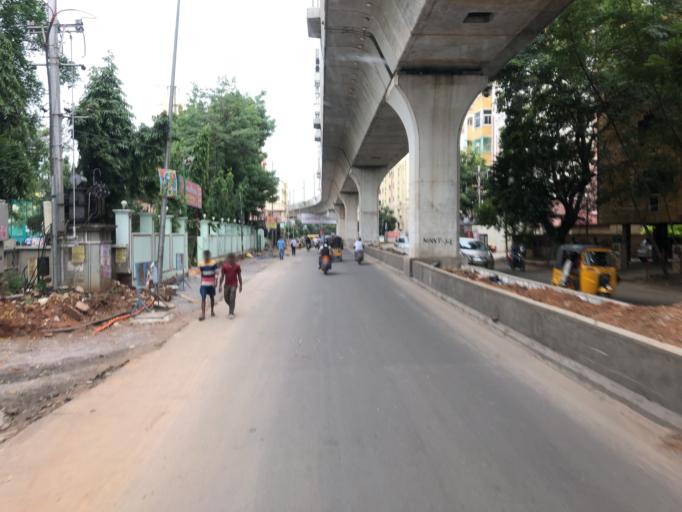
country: IN
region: Telangana
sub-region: Rangareddi
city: Kukatpalli
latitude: 17.4361
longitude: 78.4304
